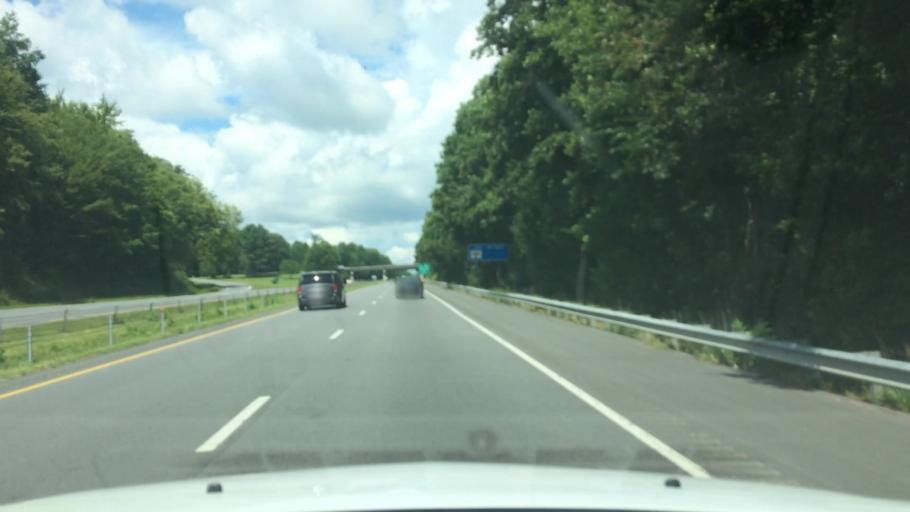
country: US
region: North Carolina
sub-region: Wilkes County
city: Wilkesboro
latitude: 36.1361
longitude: -81.1565
